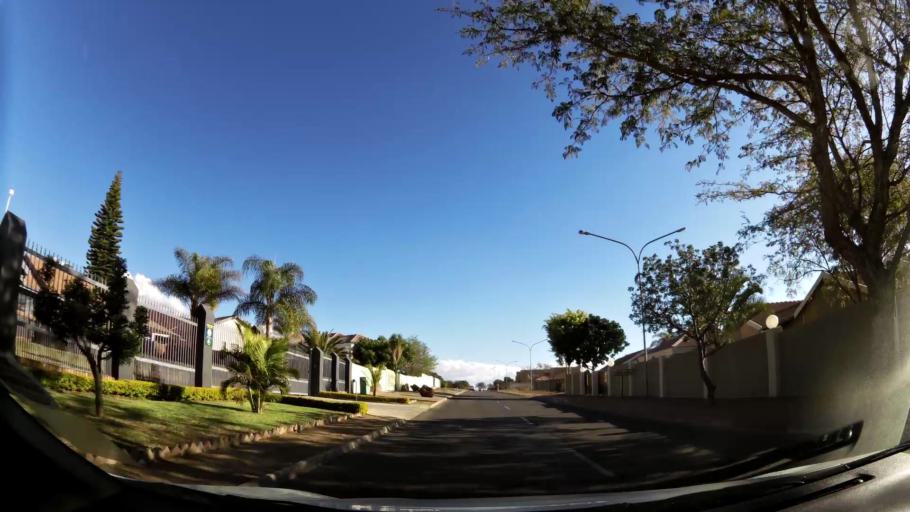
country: ZA
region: Limpopo
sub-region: Capricorn District Municipality
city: Polokwane
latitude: -23.8822
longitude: 29.4878
